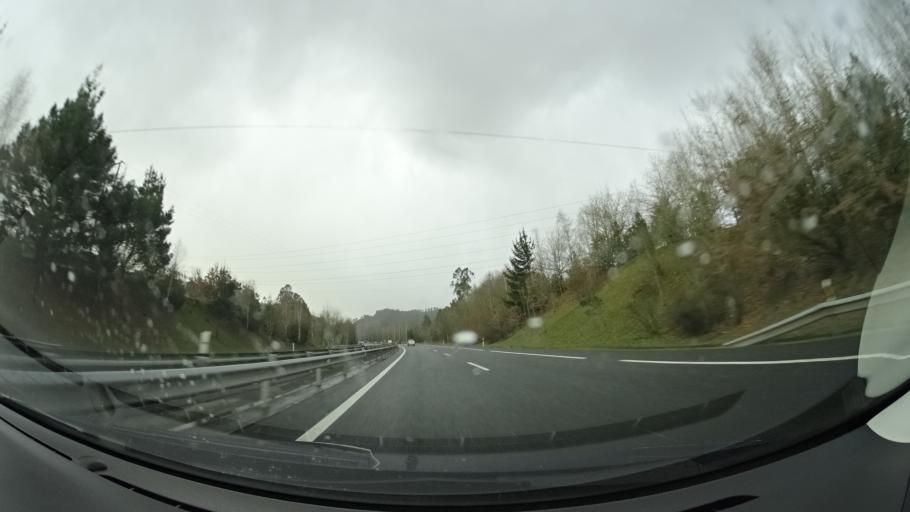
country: ES
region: Basque Country
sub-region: Bizkaia
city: Gatika
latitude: 43.3347
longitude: -2.8679
